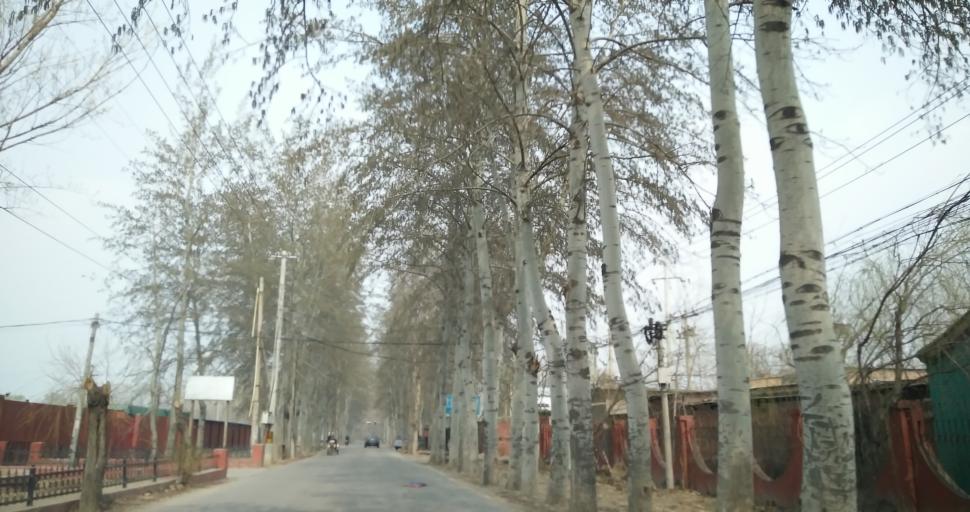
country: CN
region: Beijing
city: Qingyundian
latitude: 39.6852
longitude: 116.5061
